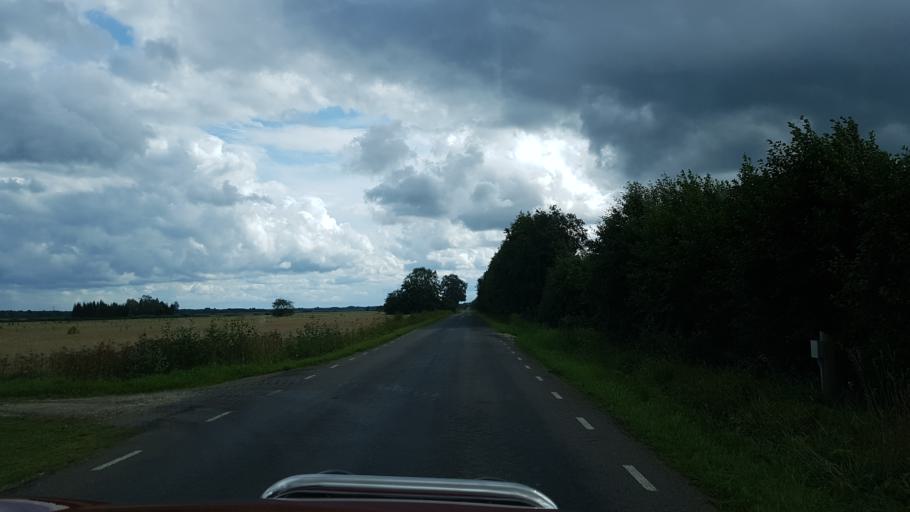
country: EE
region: Laeaene
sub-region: Lihula vald
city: Lihula
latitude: 58.7213
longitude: 23.9717
